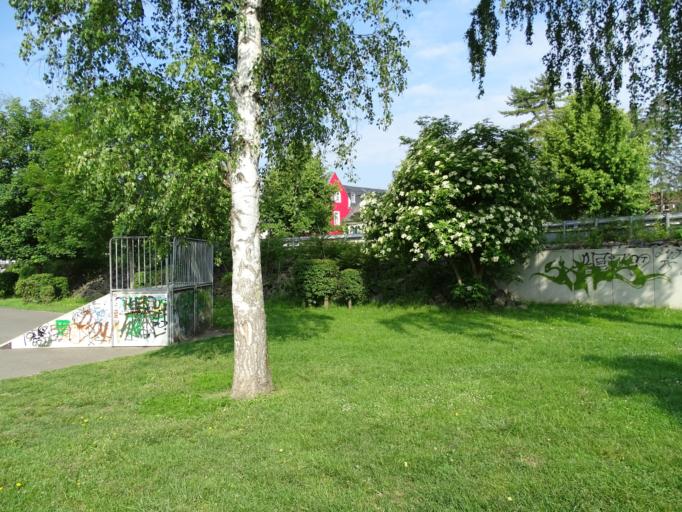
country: DE
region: Hesse
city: Geisenheim
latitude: 49.9805
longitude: 7.9688
